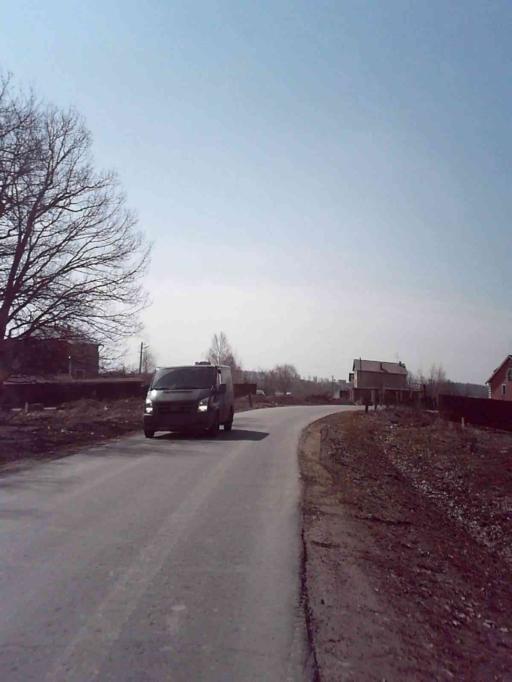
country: RU
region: Moskovskaya
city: Kommunarka
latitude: 55.5344
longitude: 37.4694
